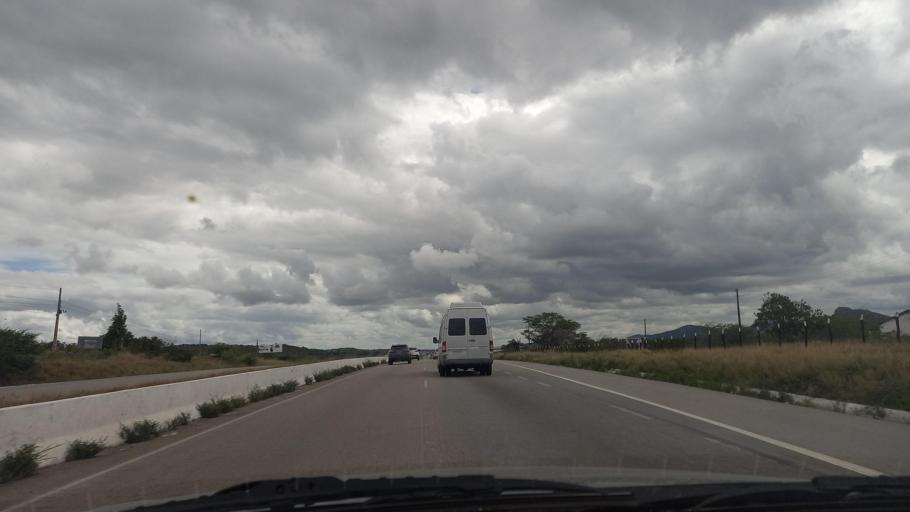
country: BR
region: Pernambuco
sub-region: Caruaru
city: Caruaru
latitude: -8.3190
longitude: -36.0658
